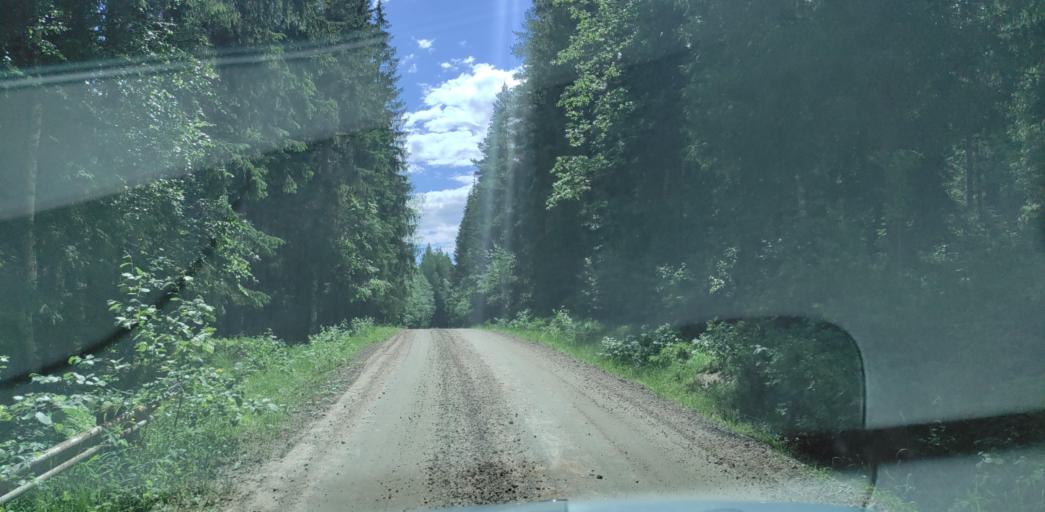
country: SE
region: Vaermland
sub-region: Sunne Kommun
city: Sunne
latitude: 60.0472
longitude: 13.2571
